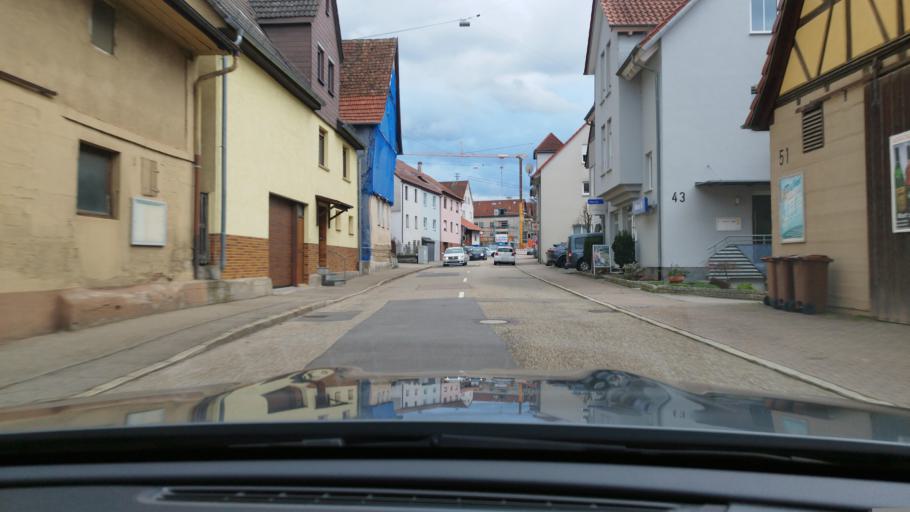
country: DE
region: Baden-Wuerttemberg
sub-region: Regierungsbezirk Stuttgart
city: Leutenbach
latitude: 48.8891
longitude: 9.3900
